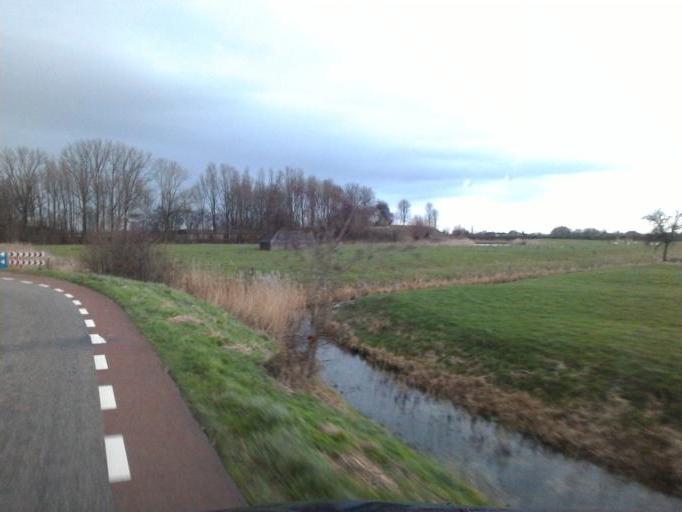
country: NL
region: Utrecht
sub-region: Gemeente Houten
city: Houten
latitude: 51.9752
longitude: 5.1592
